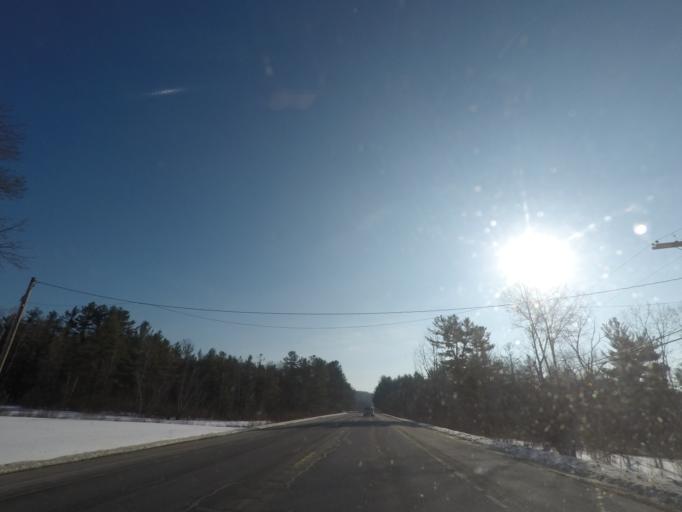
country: US
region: Massachusetts
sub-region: Berkshire County
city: Lanesborough
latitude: 42.5235
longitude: -73.3576
